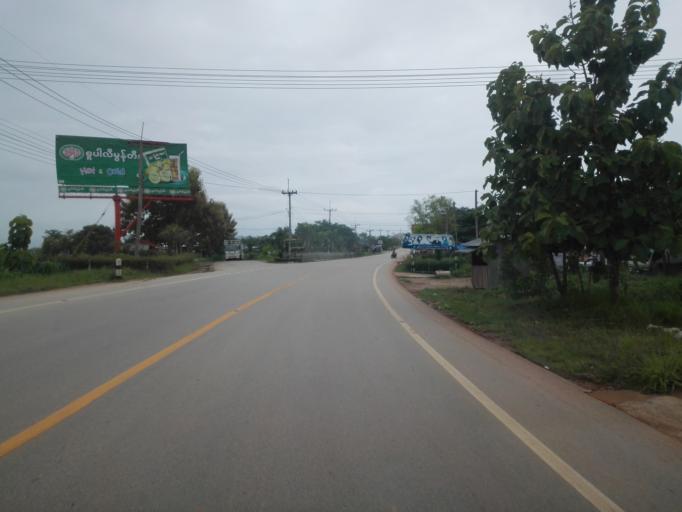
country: TH
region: Tak
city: Mae Sot
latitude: 16.6932
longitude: 98.4626
